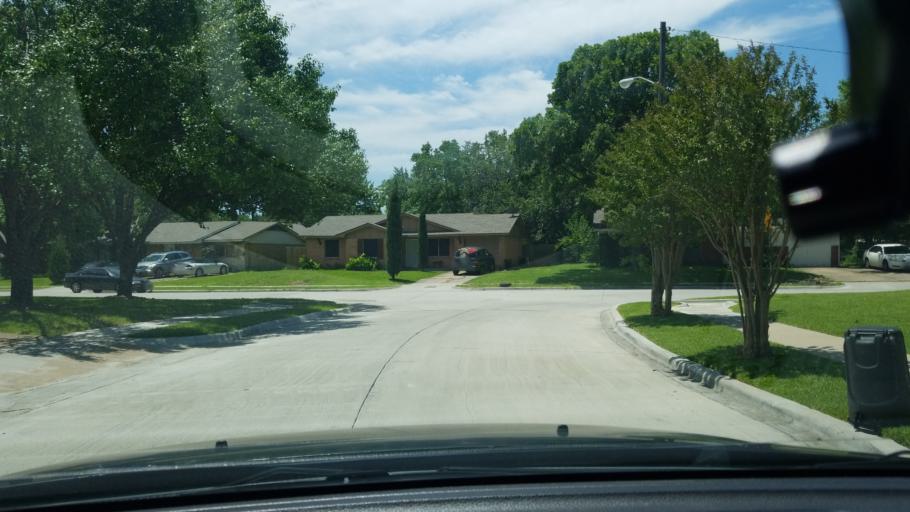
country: US
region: Texas
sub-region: Dallas County
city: Mesquite
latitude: 32.8073
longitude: -96.6537
